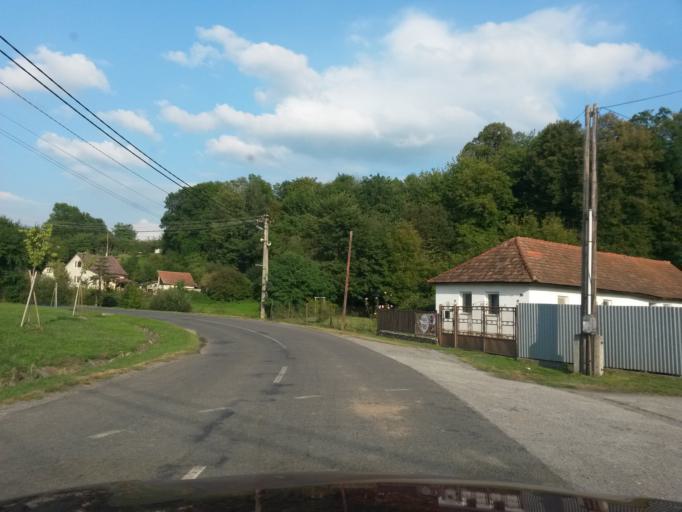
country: SK
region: Kosicky
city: Kosice
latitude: 48.7662
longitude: 21.4441
